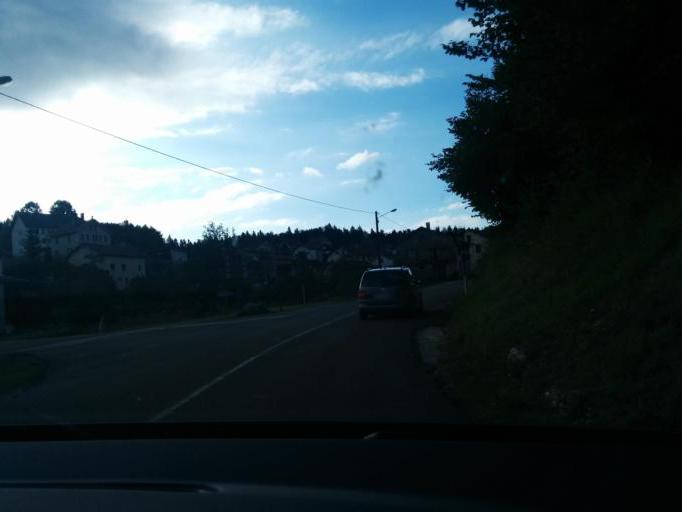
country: FR
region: Franche-Comte
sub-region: Departement du Jura
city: Saint-Lupicin
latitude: 46.4600
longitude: 5.7959
